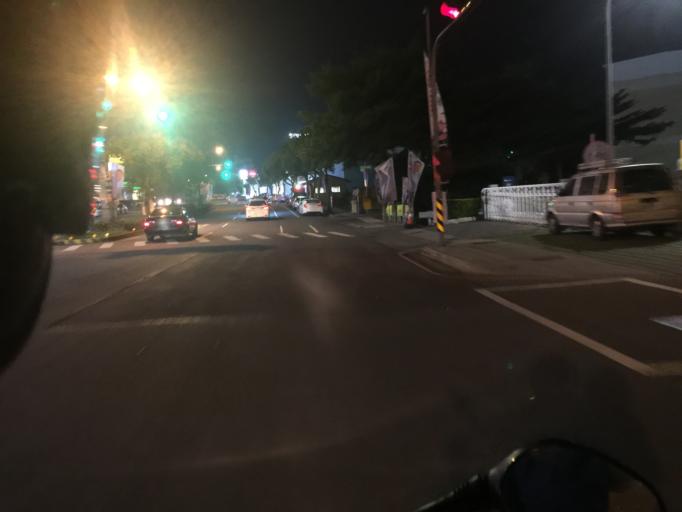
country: TW
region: Taiwan
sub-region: Miaoli
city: Miaoli
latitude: 24.5750
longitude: 120.8183
